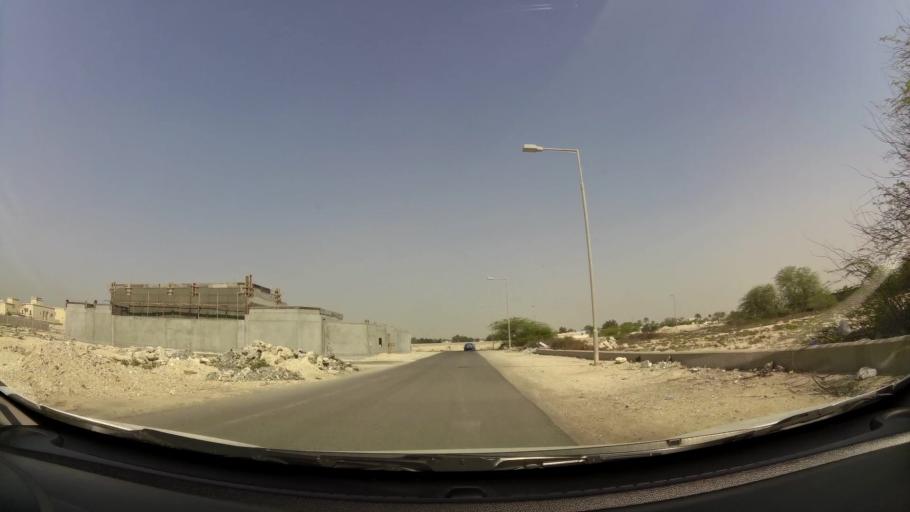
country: BH
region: Manama
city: Jidd Hafs
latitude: 26.2010
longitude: 50.4650
